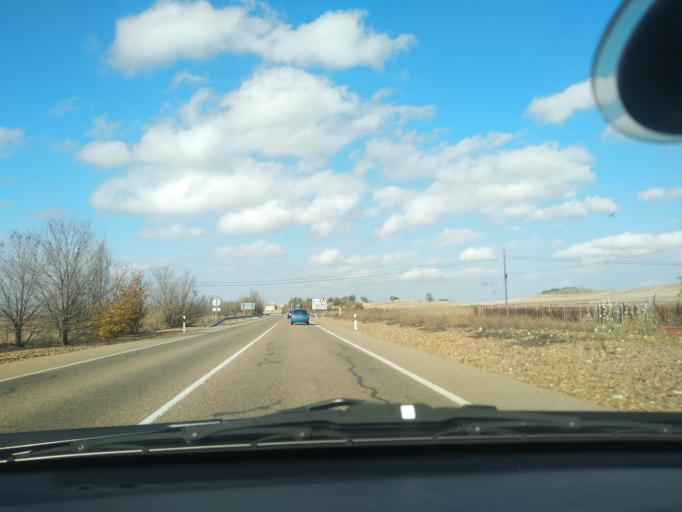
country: ES
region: Castille and Leon
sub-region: Provincia de Valladolid
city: Medina de Rioseco
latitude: 41.8656
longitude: -5.0256
